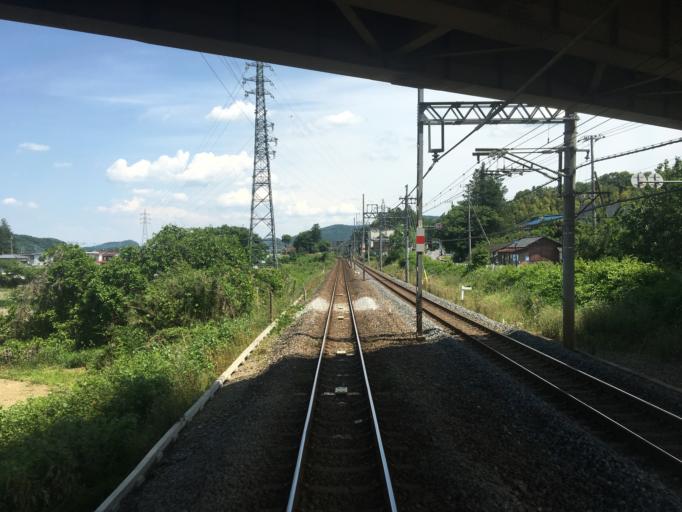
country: JP
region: Saitama
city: Ogawa
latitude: 36.0649
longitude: 139.2477
